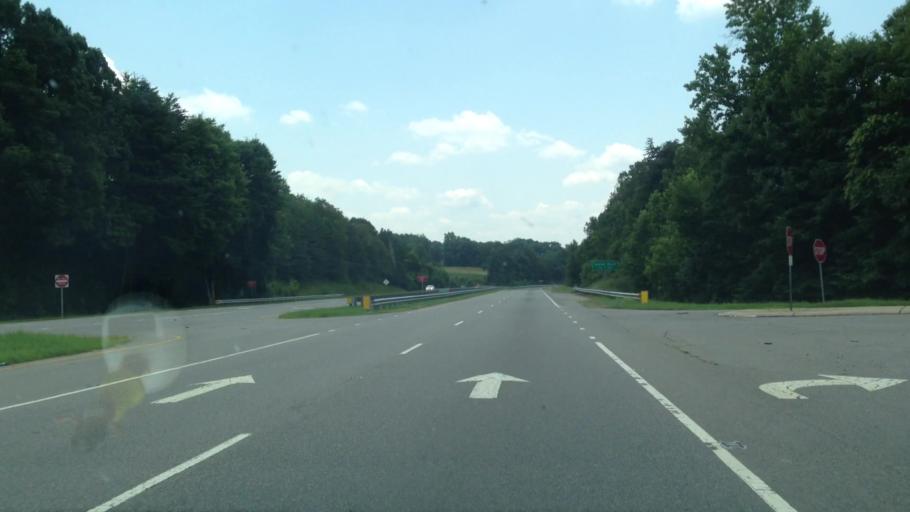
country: US
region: North Carolina
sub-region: Rockingham County
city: Stoneville
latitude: 36.5201
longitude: -79.9176
